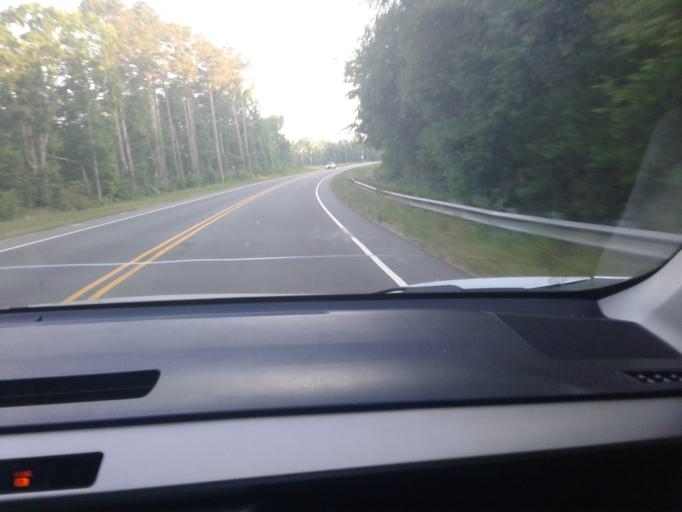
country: US
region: North Carolina
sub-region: Harnett County
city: Lillington
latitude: 35.4295
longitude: -78.8253
